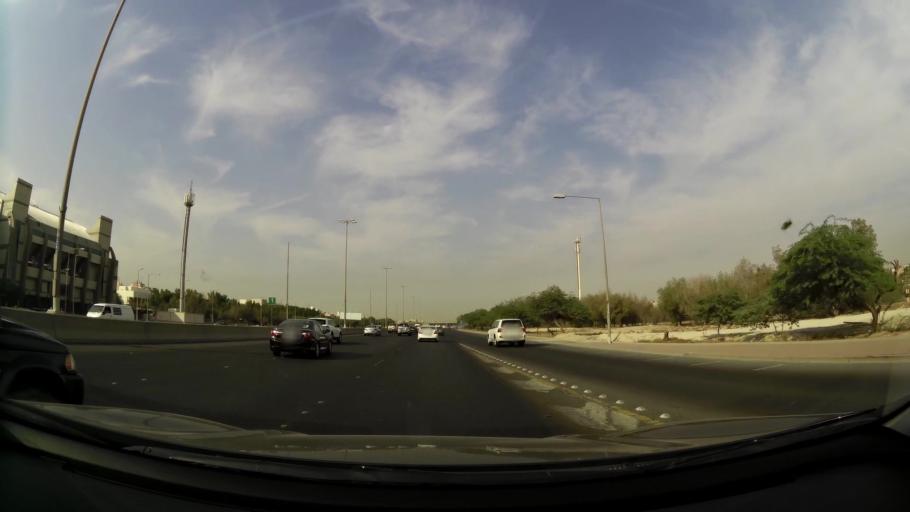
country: KW
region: Mubarak al Kabir
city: Sabah as Salim
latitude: 29.2663
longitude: 48.0744
